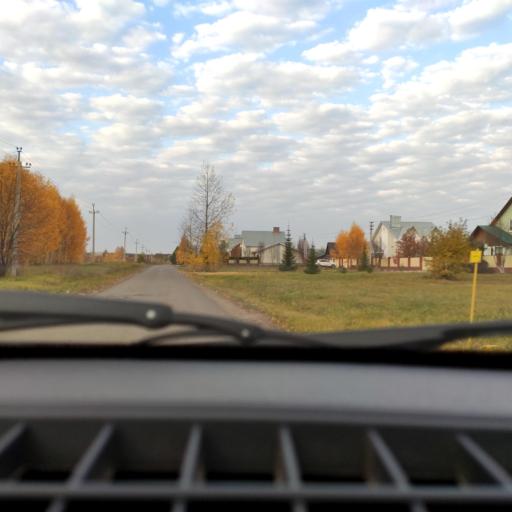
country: RU
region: Bashkortostan
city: Avdon
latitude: 54.6937
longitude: 55.7975
